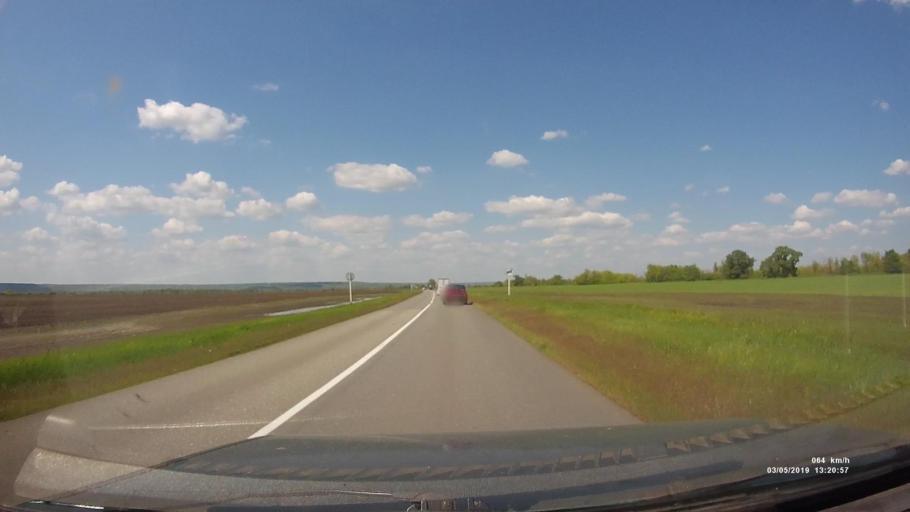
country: RU
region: Rostov
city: Semikarakorsk
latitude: 47.5505
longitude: 40.7500
